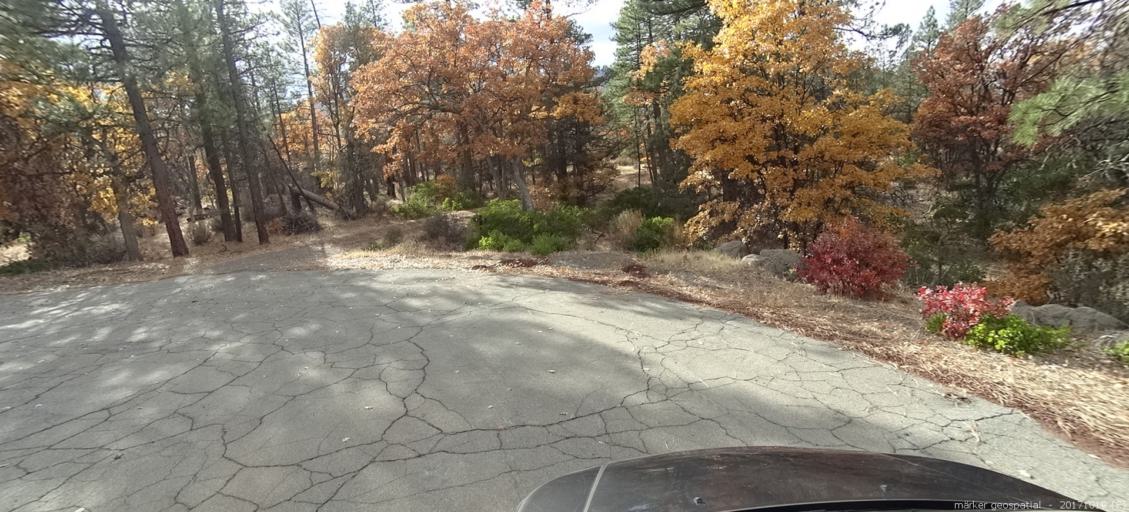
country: US
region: California
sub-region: Shasta County
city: Burney
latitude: 40.9622
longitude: -121.4424
